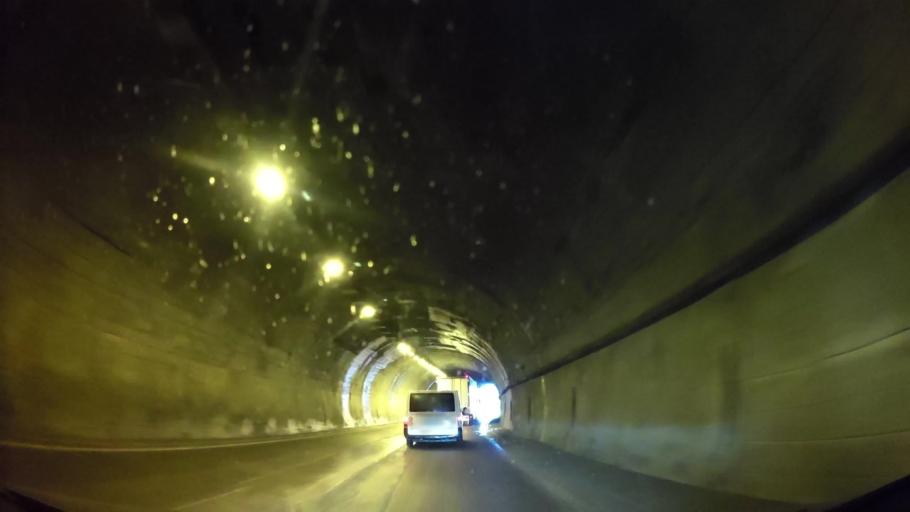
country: RS
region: Central Serbia
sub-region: Pcinjski Okrug
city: Vladicin Han
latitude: 42.7269
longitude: 22.0671
